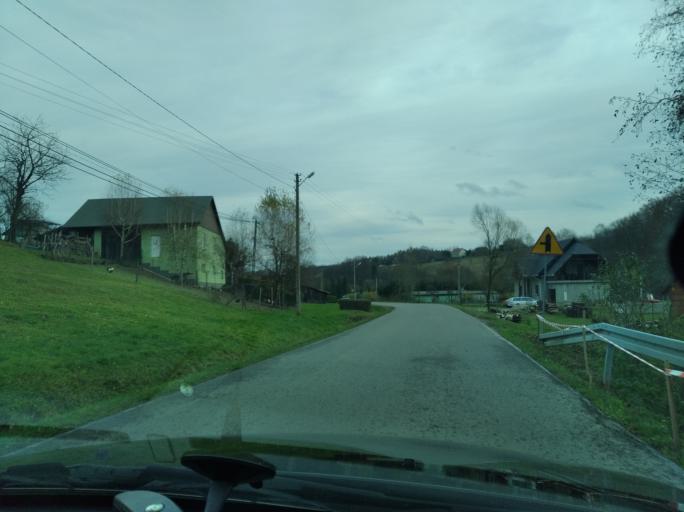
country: PL
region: Subcarpathian Voivodeship
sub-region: Powiat ropczycko-sedziszowski
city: Iwierzyce
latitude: 49.9470
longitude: 21.7340
